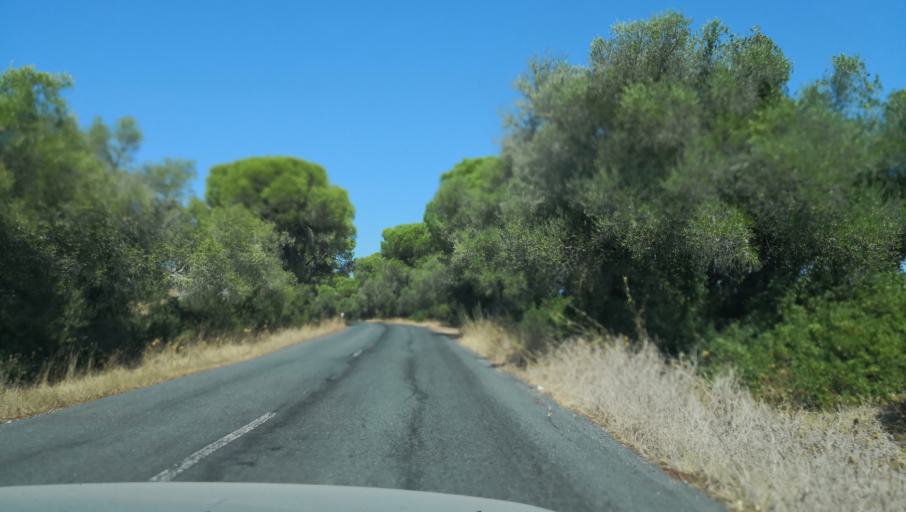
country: PT
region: Setubal
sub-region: Alcacer do Sal
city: Alcacer do Sal
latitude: 38.2928
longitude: -8.4037
